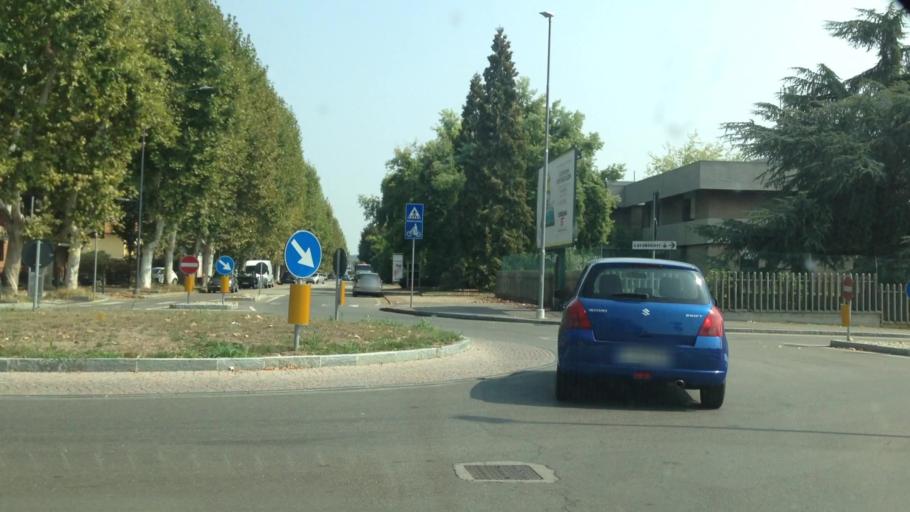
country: IT
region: Piedmont
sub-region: Provincia di Asti
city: Asti
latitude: 44.9046
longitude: 8.2249
